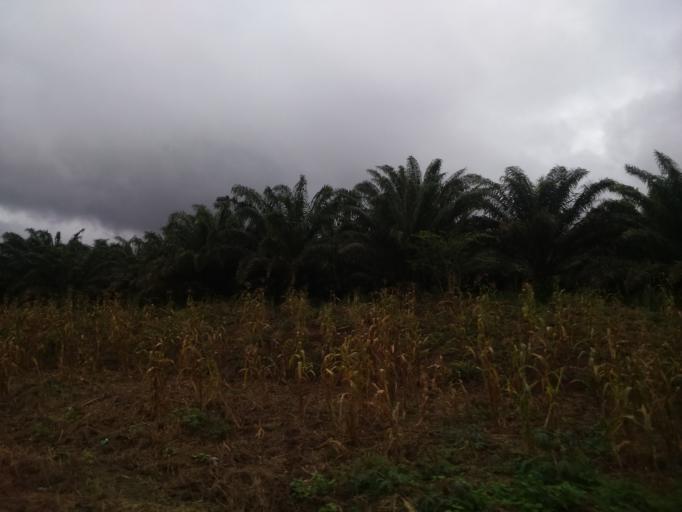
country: CI
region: Sud-Comoe
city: Adiake
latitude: 5.3004
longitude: -3.3496
